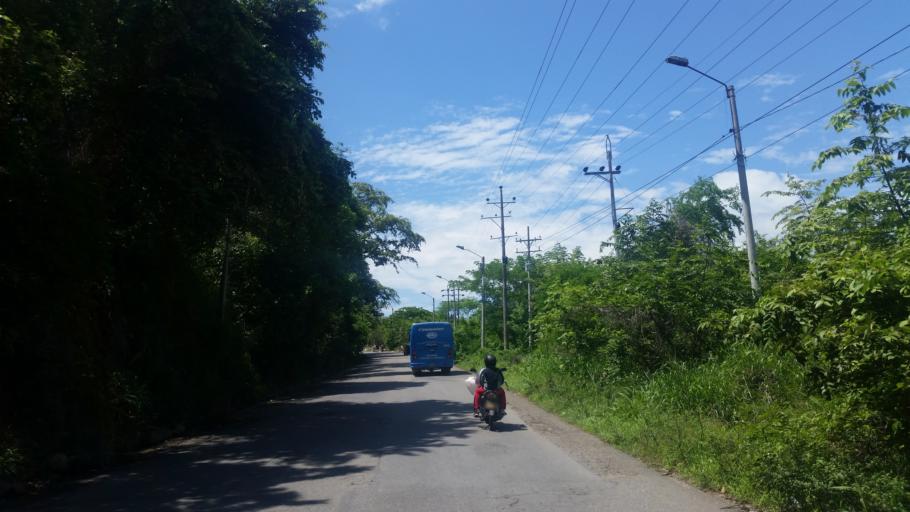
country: CO
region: Huila
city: Neiva
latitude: 2.9819
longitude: -75.2828
